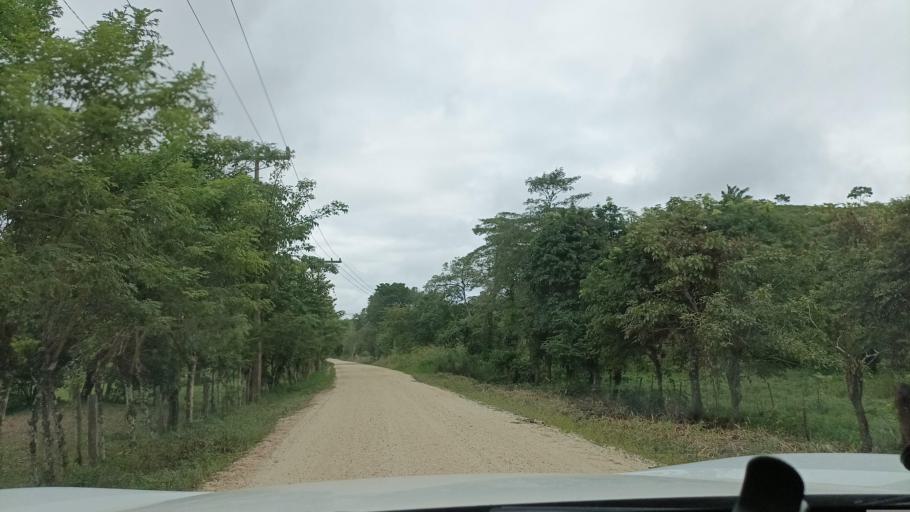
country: MX
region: Veracruz
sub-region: Moloacan
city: Cuichapa
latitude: 17.8415
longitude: -94.3588
